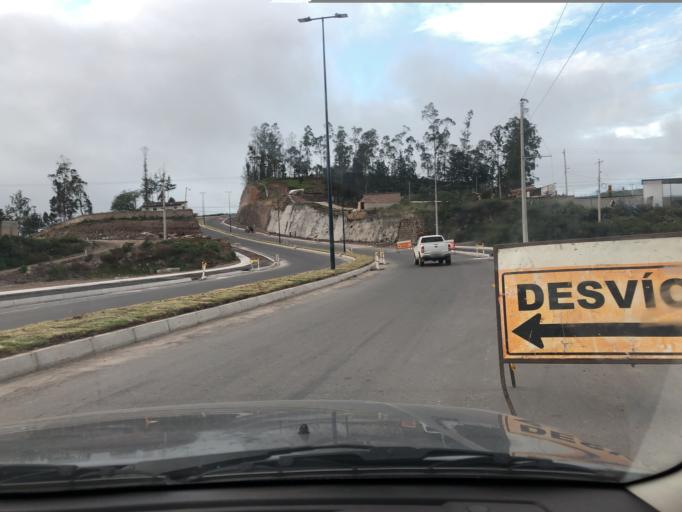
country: EC
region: Imbabura
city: Ibarra
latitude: 0.3567
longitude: -78.1392
